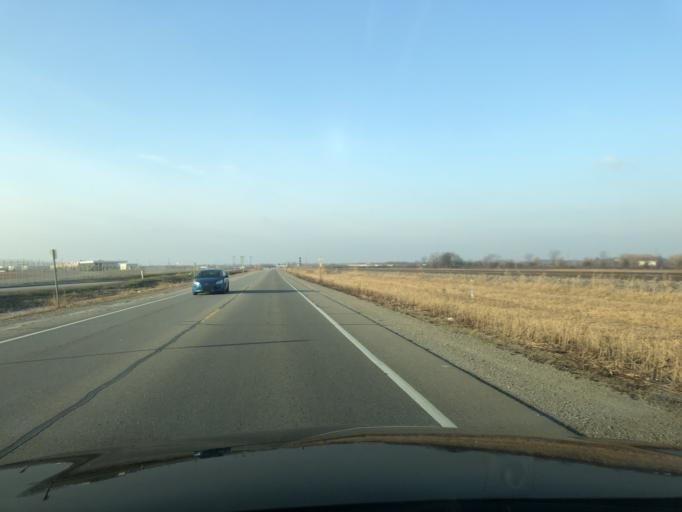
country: US
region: Michigan
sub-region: Wayne County
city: Romulus
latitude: 42.2346
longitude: -83.3492
